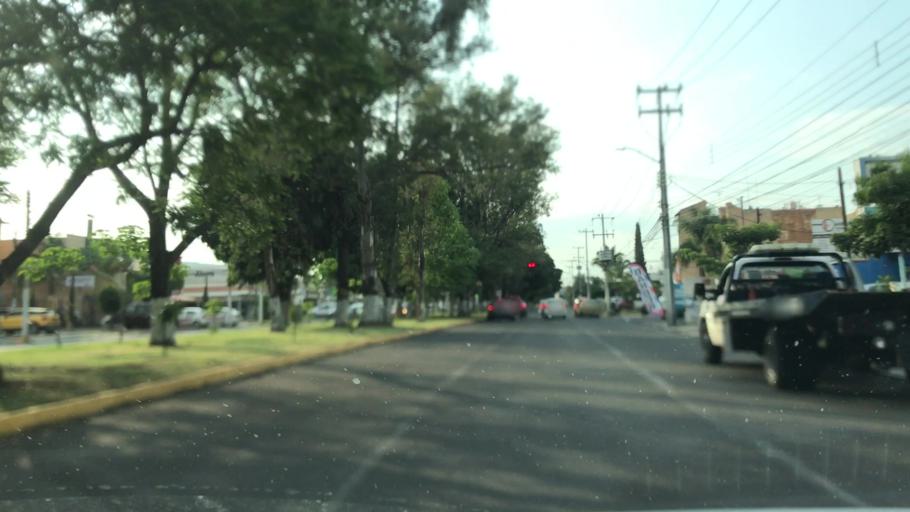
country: MX
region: Jalisco
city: Guadalajara
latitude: 20.6311
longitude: -103.4240
